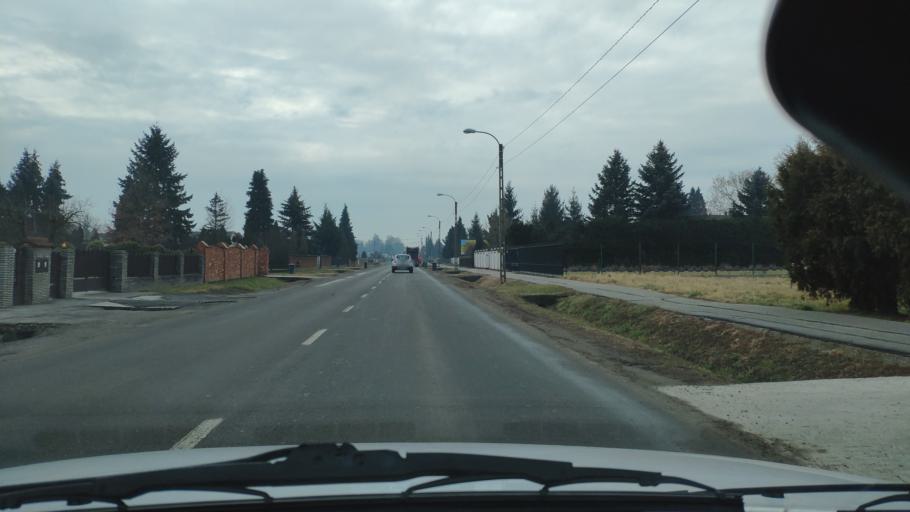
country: HU
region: Zala
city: Nagykanizsa
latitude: 46.4861
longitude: 16.9852
